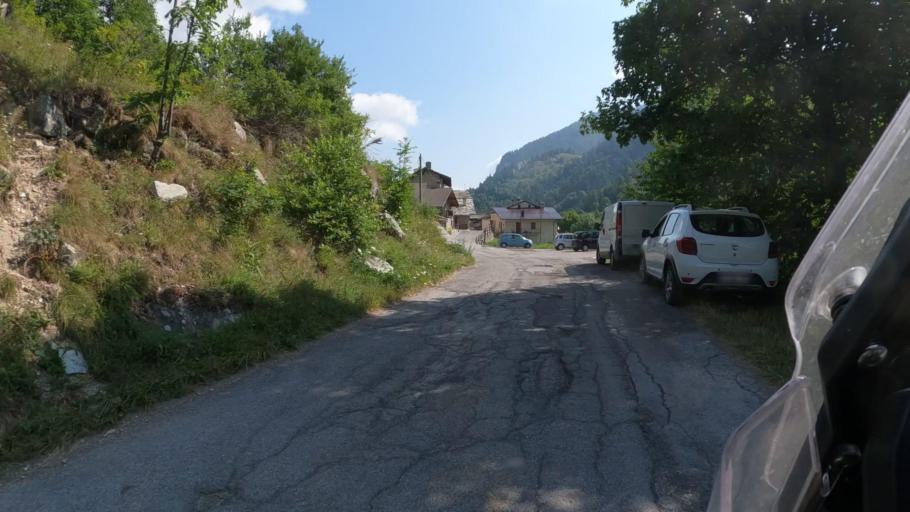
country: IT
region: Piedmont
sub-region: Provincia di Cuneo
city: Canosio
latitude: 44.4345
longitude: 7.0554
